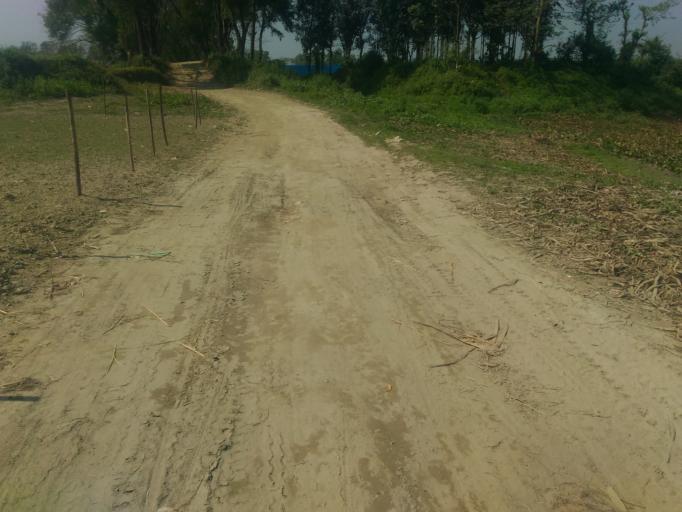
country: BD
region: Dhaka
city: Azimpur
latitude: 23.7848
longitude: 90.2314
